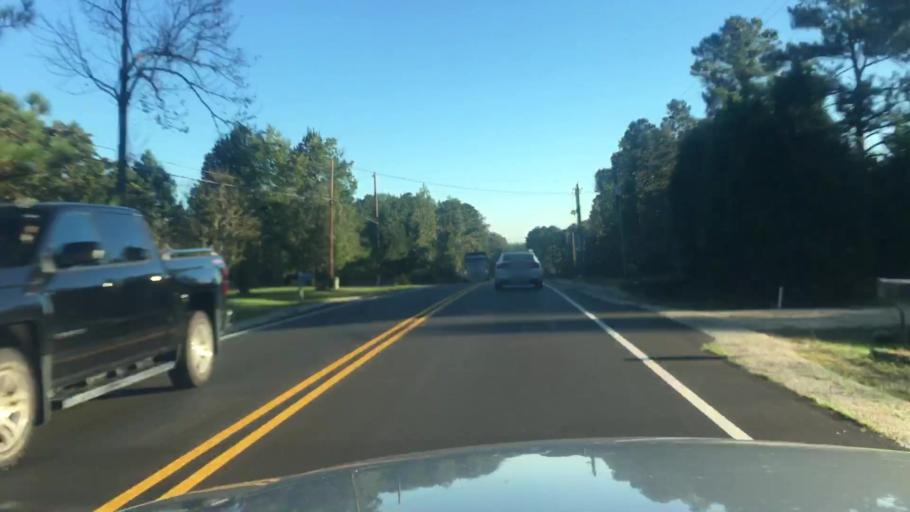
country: US
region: North Carolina
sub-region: Harnett County
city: Walkertown
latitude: 35.3375
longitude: -78.8581
